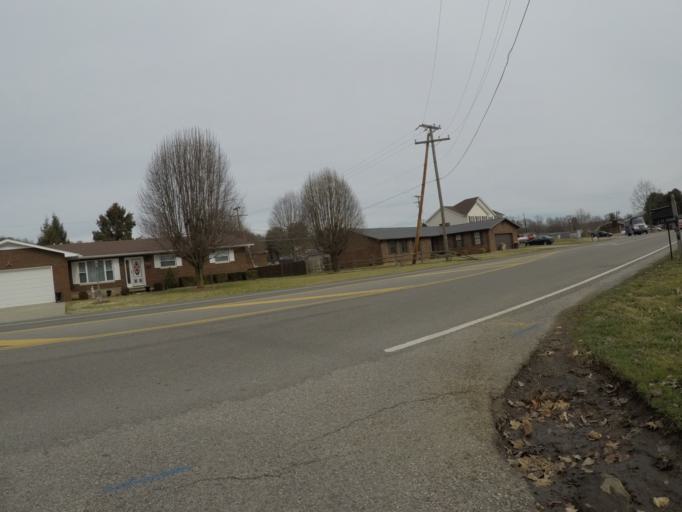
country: US
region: West Virginia
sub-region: Cabell County
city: Pea Ridge
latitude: 38.4537
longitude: -82.3390
